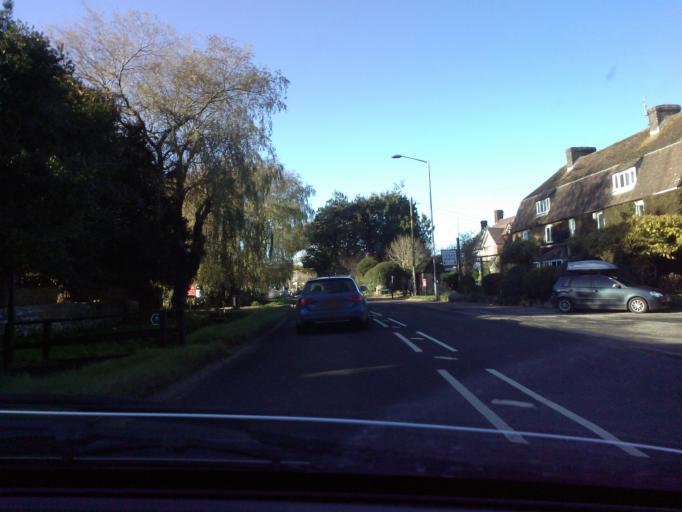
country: GB
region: England
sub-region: Dorset
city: Chickerell
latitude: 50.7129
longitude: -2.5411
